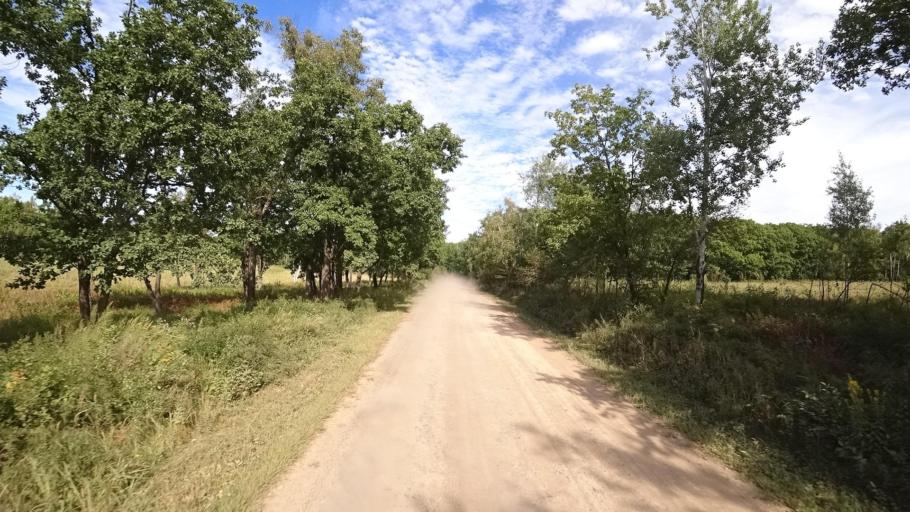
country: RU
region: Primorskiy
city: Dostoyevka
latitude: 44.3752
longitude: 133.5300
